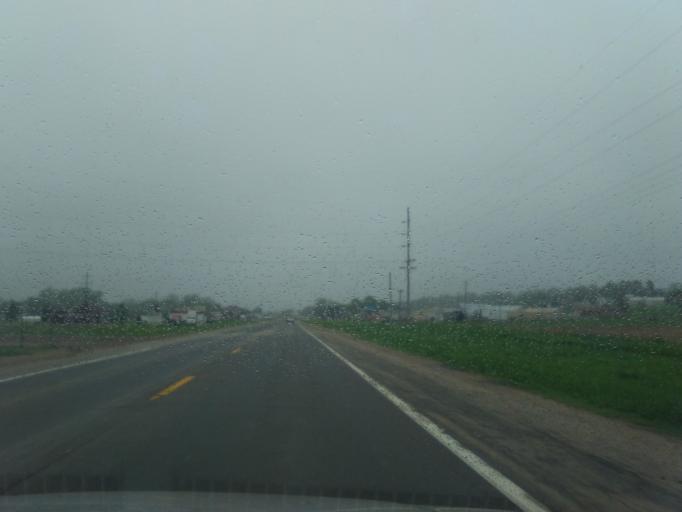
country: US
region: Nebraska
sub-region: Cuming County
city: Wisner
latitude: 41.9790
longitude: -96.9021
